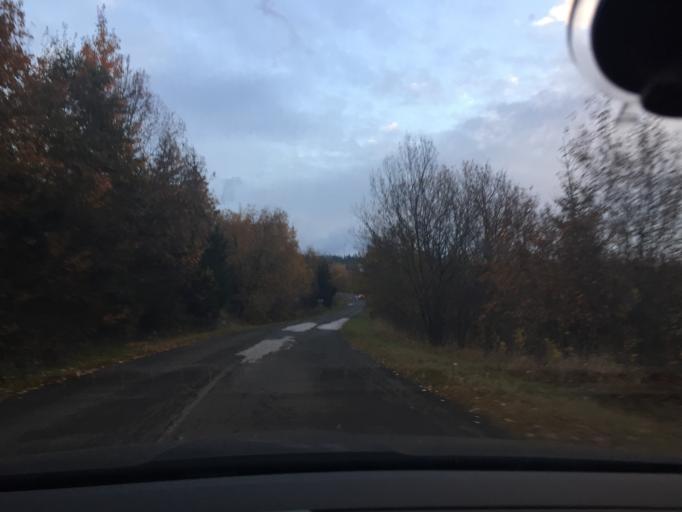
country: SK
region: Presovsky
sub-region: Okres Poprad
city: Vysoke Tatry
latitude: 49.1366
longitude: 20.2380
